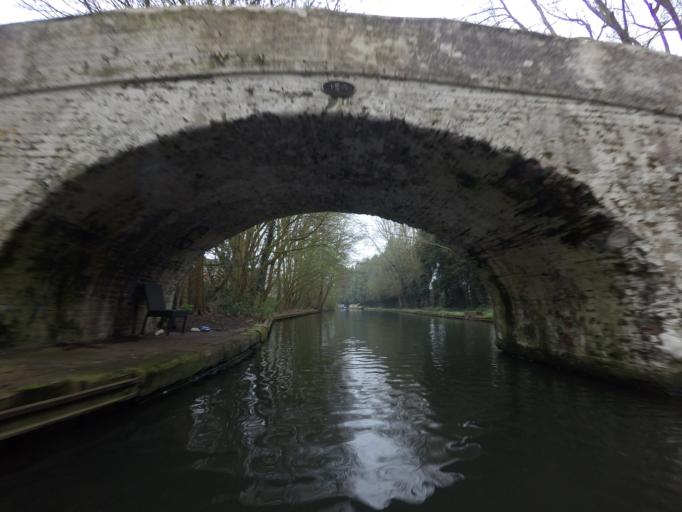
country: GB
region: England
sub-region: Hertfordshire
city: Kings Langley
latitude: 51.7324
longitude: -0.4594
